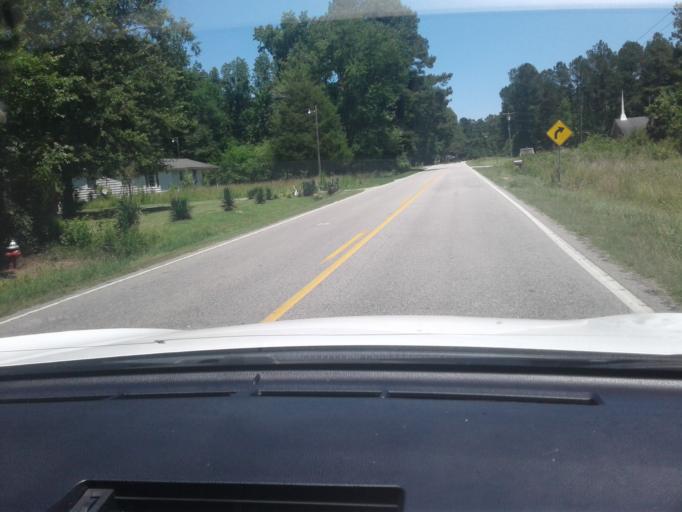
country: US
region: North Carolina
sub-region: Harnett County
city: Erwin
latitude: 35.3176
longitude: -78.7117
